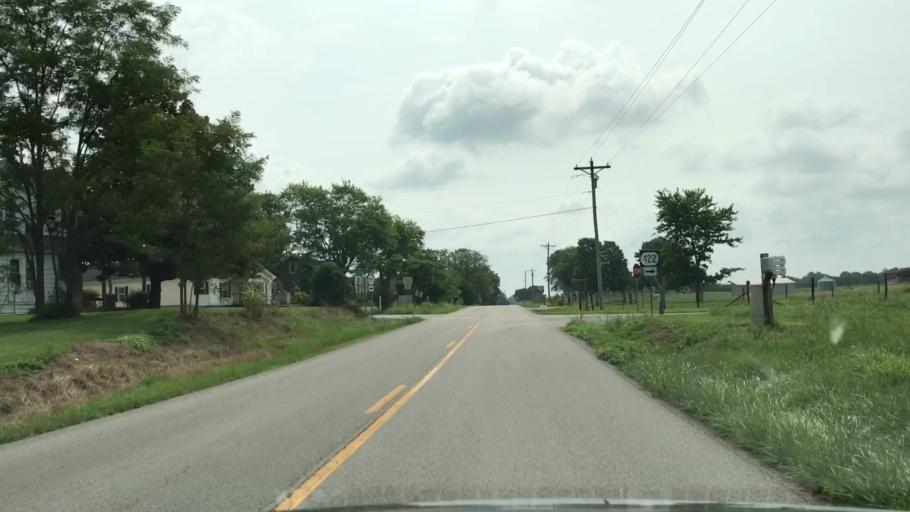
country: US
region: Kentucky
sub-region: Edmonson County
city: Brownsville
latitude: 37.1330
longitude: -86.1706
